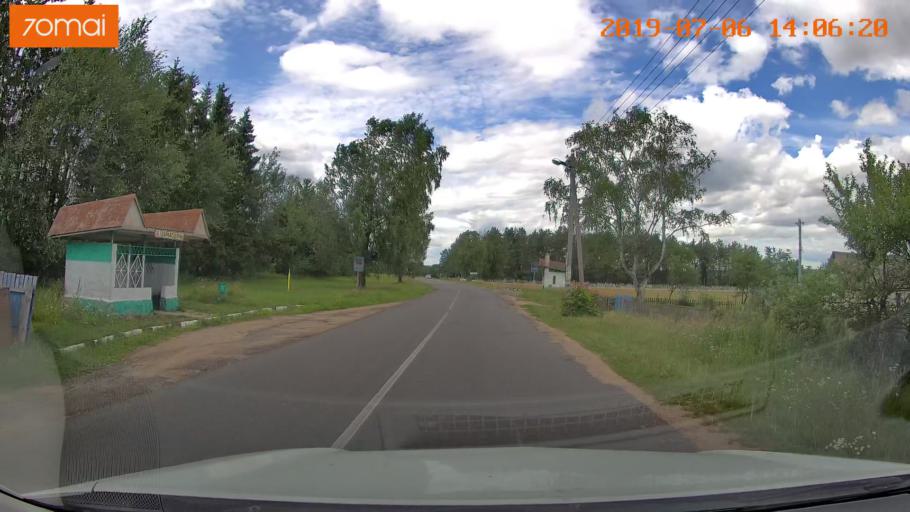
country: BY
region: Minsk
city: Ivyanyets
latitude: 53.8615
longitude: 26.7831
